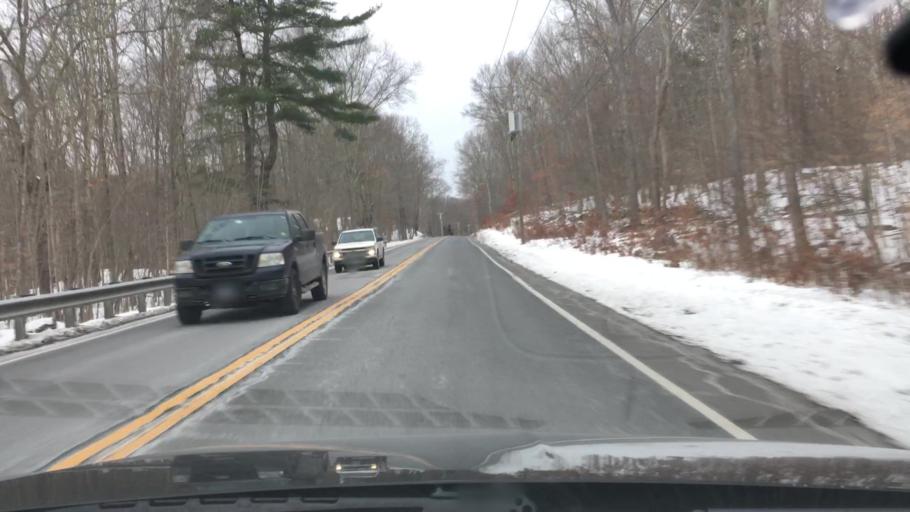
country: US
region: Connecticut
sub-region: Tolland County
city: Tolland
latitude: 41.8408
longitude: -72.3189
